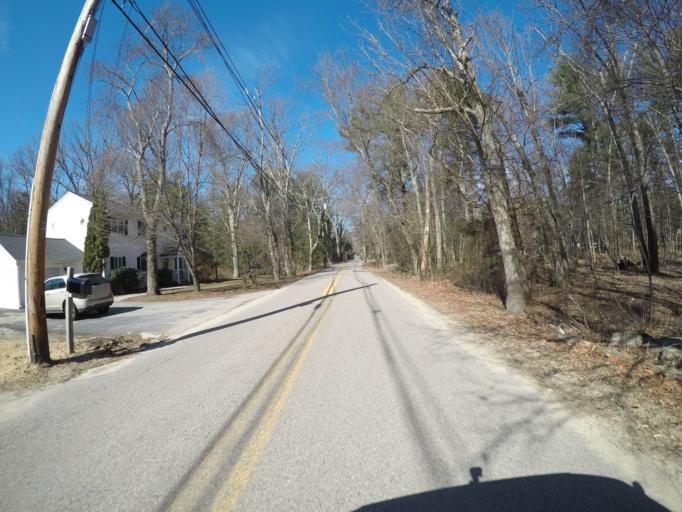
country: US
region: Massachusetts
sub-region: Norfolk County
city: Sharon
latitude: 42.0951
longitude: -71.1576
